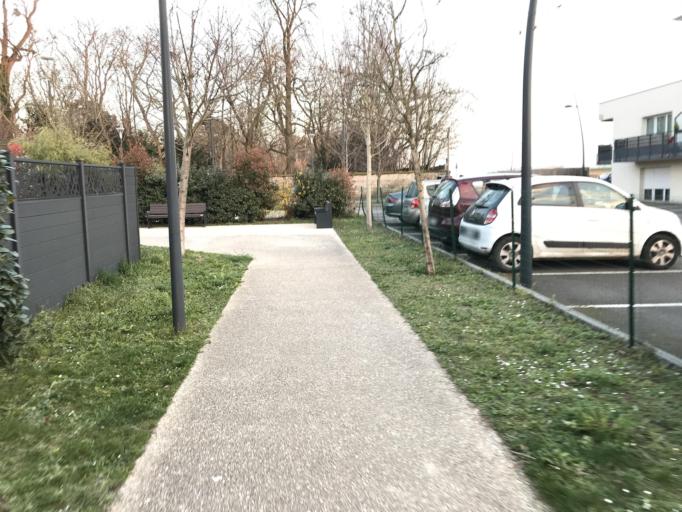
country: FR
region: Ile-de-France
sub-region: Departement de l'Essonne
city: Ballainvilliers
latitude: 48.6725
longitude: 2.2916
